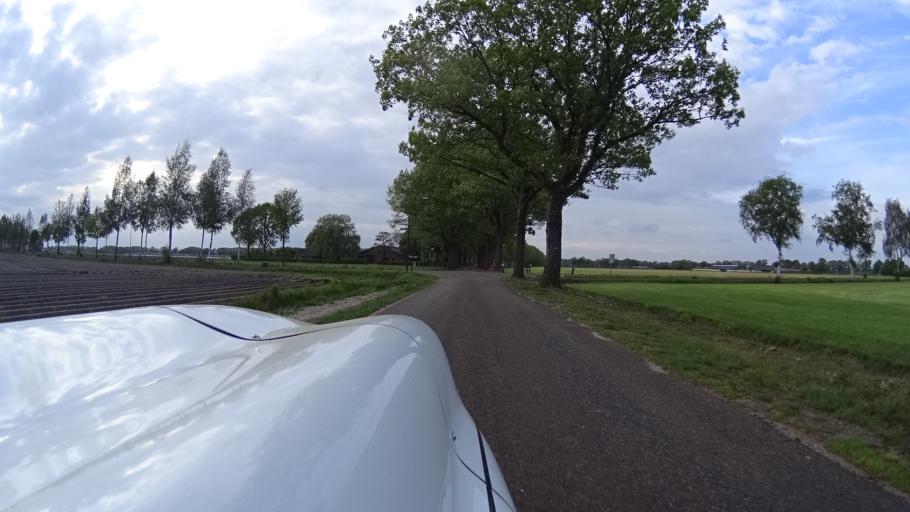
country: NL
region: North Brabant
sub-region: Gemeente Mill en Sint Hubert
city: Wilbertoord
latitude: 51.5931
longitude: 5.7892
